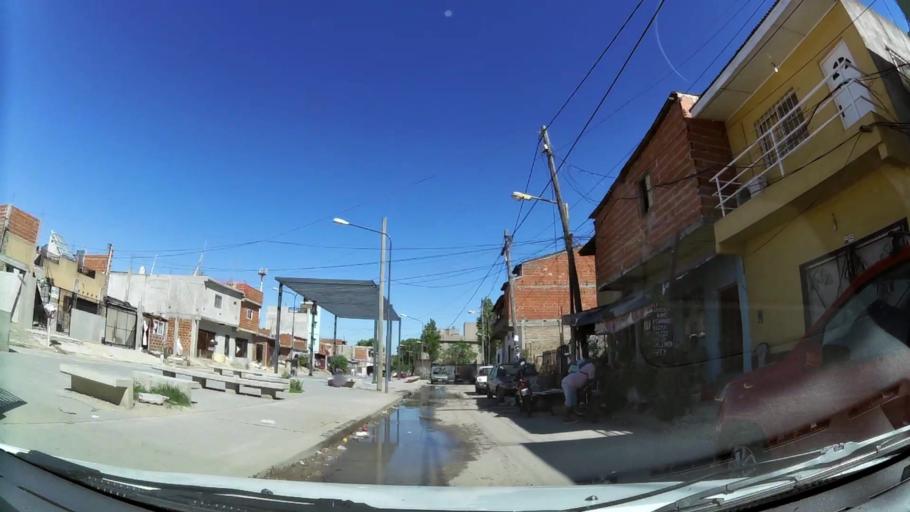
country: AR
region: Buenos Aires
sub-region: Partido de General San Martin
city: General San Martin
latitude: -34.5324
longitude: -58.5795
